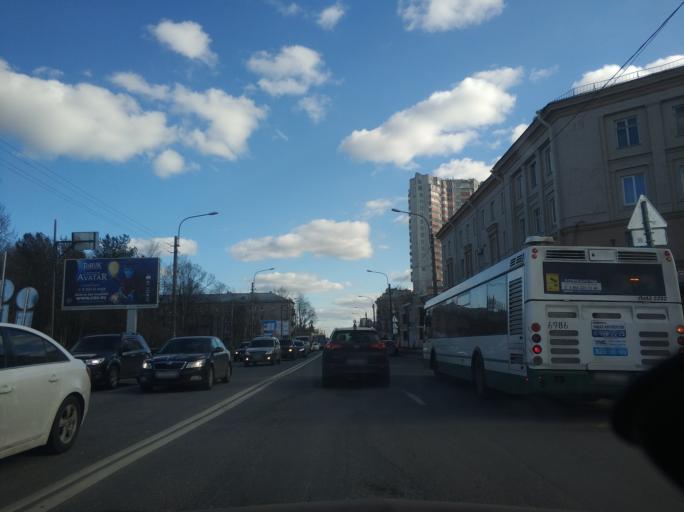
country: RU
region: St.-Petersburg
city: Krasnogvargeisky
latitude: 59.9615
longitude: 30.4891
